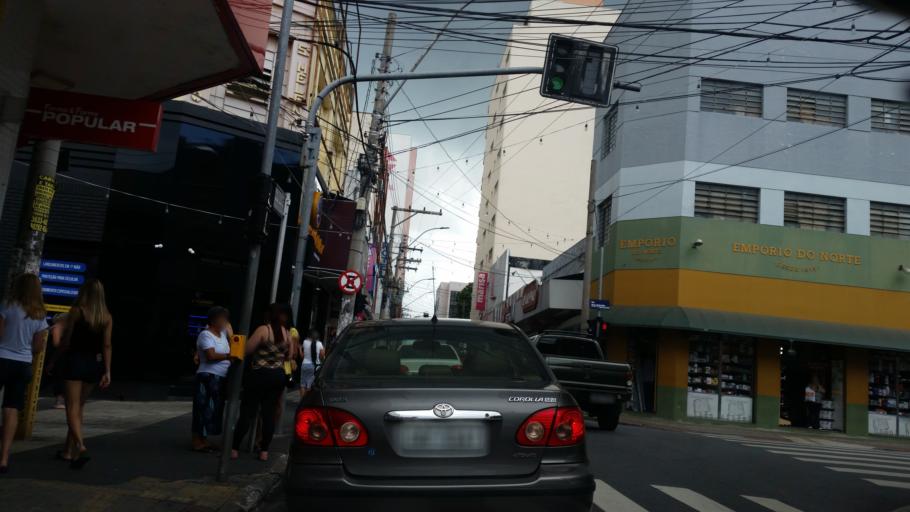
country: BR
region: Sao Paulo
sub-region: Taubate
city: Taubate
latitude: -23.0262
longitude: -45.5544
